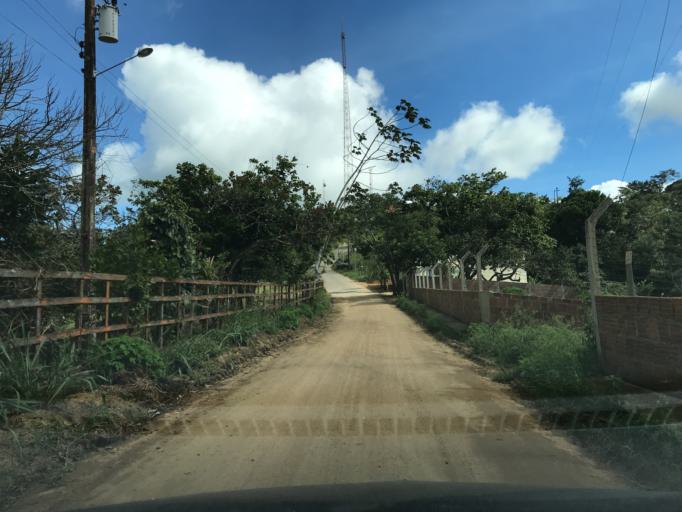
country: BR
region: Pernambuco
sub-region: Bezerros
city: Bezerros
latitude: -8.1629
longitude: -35.7664
